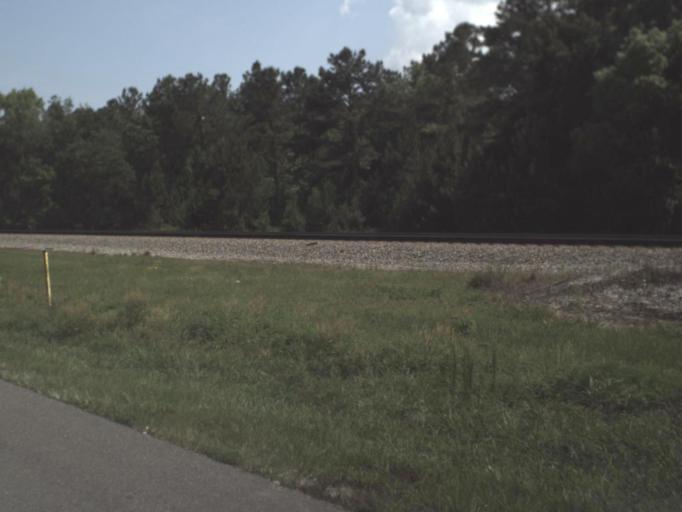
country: US
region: Florida
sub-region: Saint Johns County
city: Fruit Cove
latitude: 30.1421
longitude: -81.5169
